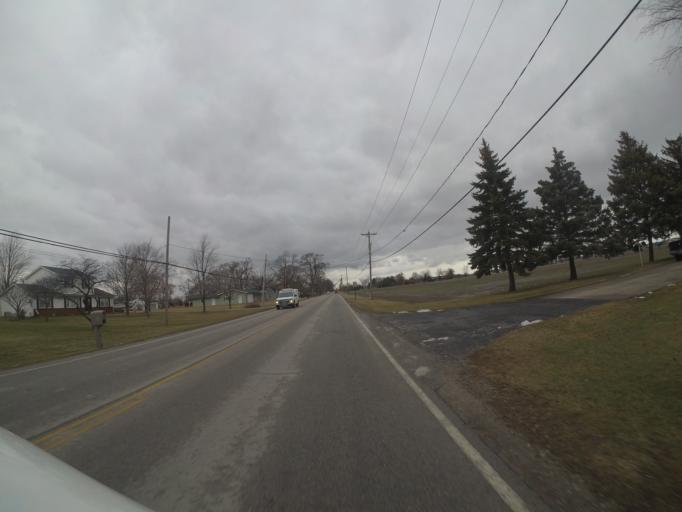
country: US
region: Ohio
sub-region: Wood County
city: Walbridge
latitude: 41.5737
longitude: -83.5121
